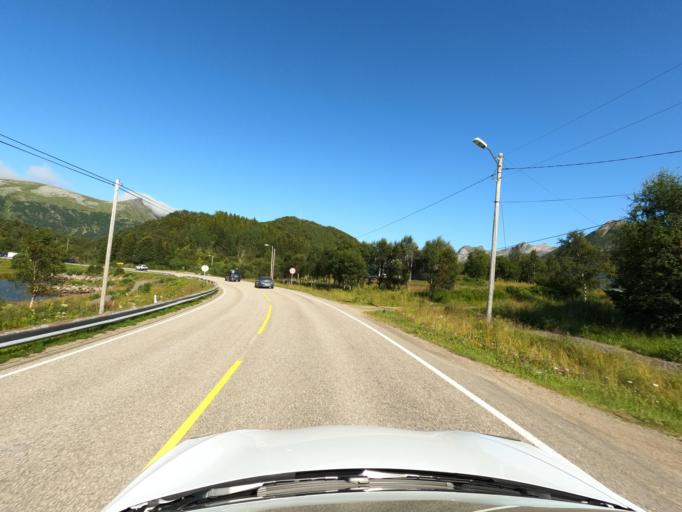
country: NO
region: Nordland
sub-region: Vagan
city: Kabelvag
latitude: 68.2402
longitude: 14.2800
